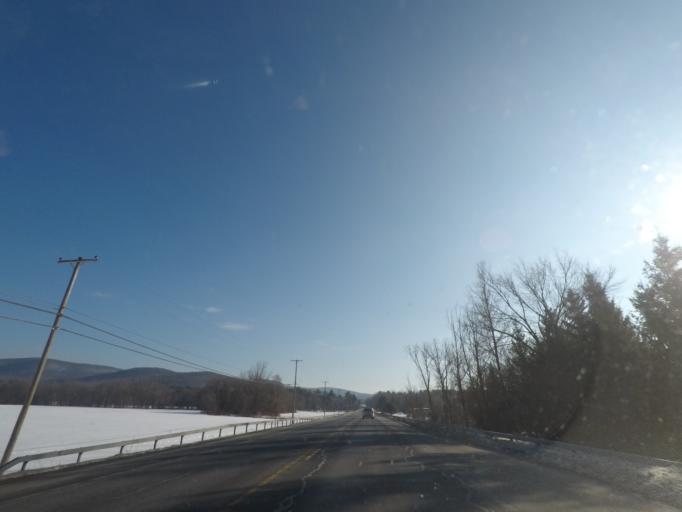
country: US
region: Massachusetts
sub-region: Berkshire County
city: Lanesborough
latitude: 42.5399
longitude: -73.3603
